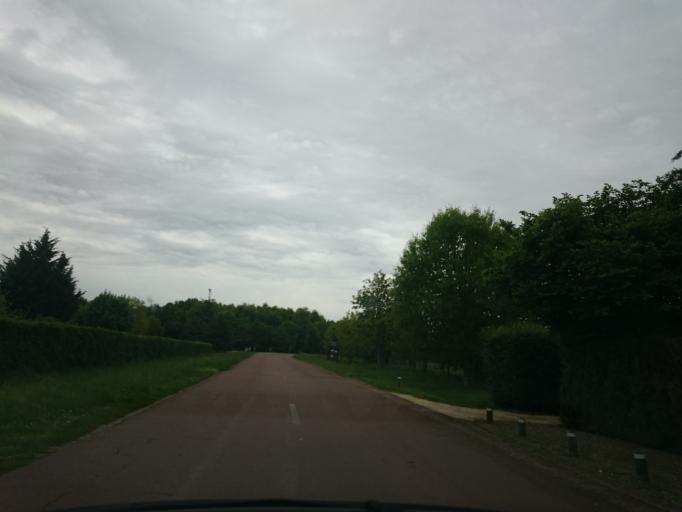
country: FR
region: Centre
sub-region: Departement du Loir-et-Cher
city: Muides-sur-Loire
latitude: 47.6576
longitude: 1.5341
